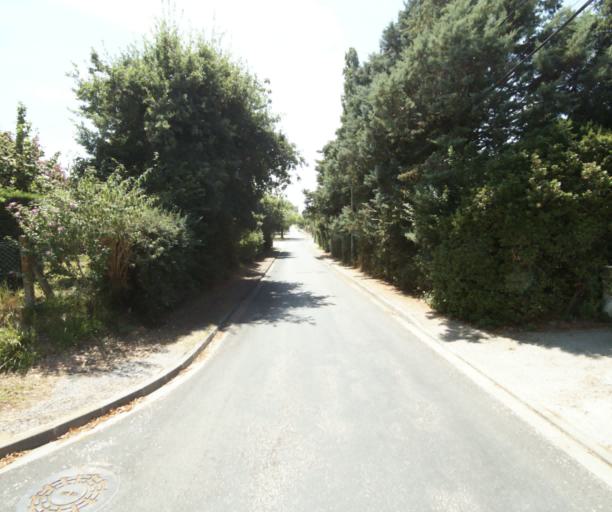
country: FR
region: Midi-Pyrenees
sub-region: Departement de la Haute-Garonne
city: Revel
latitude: 43.4896
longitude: 2.0185
